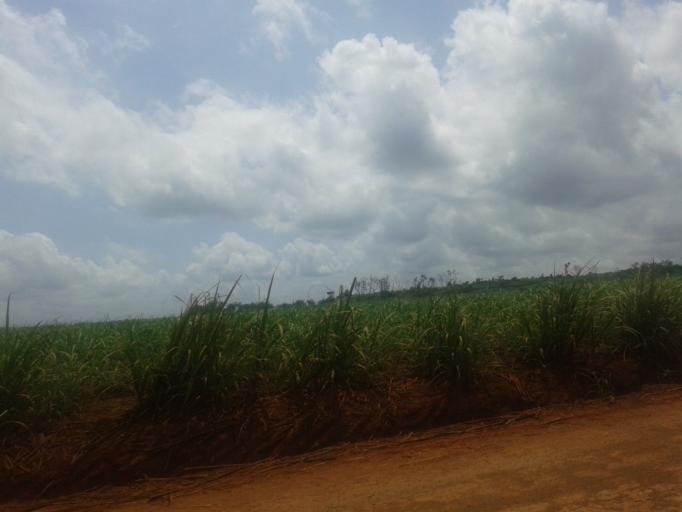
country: CM
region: Centre
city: Mbandjok
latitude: 4.4464
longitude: 11.9545
